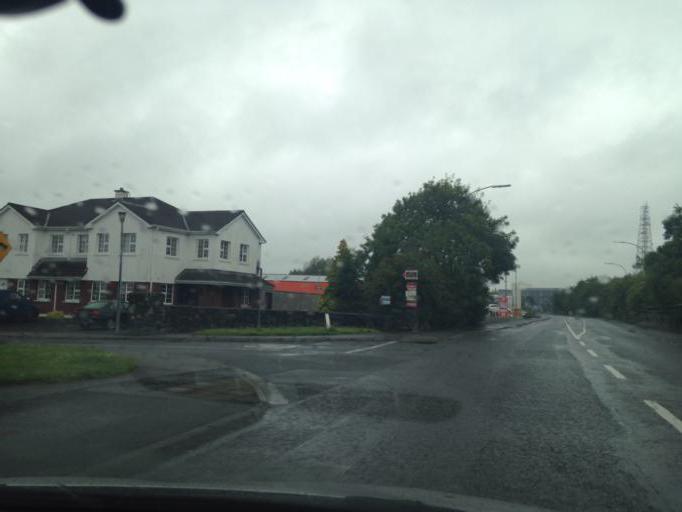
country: IE
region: Connaught
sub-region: County Galway
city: Gaillimh
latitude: 53.2878
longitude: -9.0267
